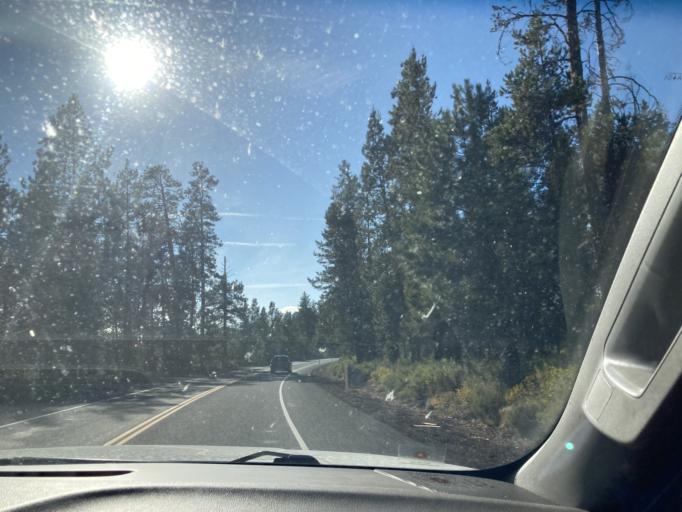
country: US
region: Oregon
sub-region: Deschutes County
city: Three Rivers
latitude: 43.8158
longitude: -121.4920
